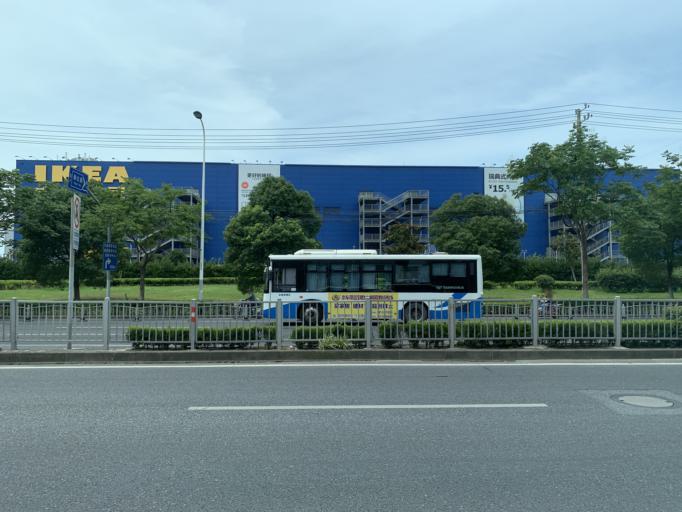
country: CN
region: Shanghai Shi
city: Kangqiao
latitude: 31.1621
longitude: 121.5596
